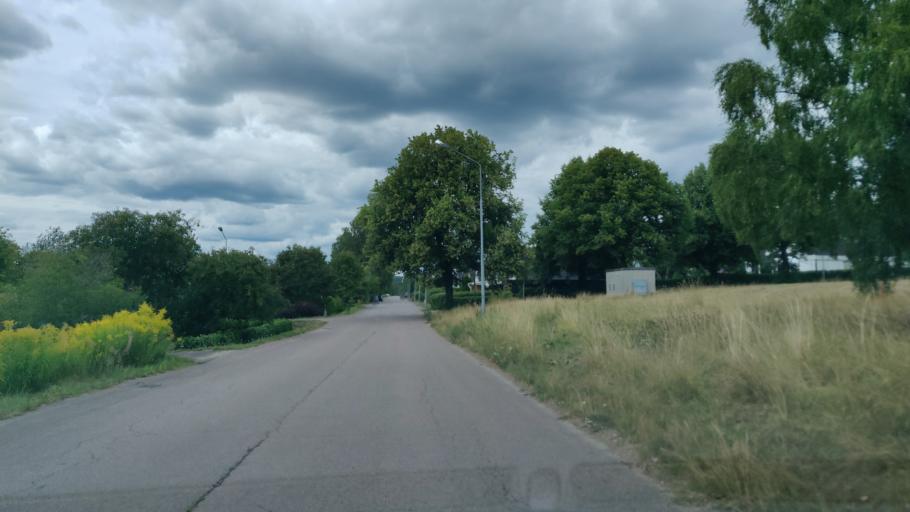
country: SE
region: Vaermland
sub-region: Hagfors Kommun
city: Hagfors
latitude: 60.0367
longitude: 13.6880
